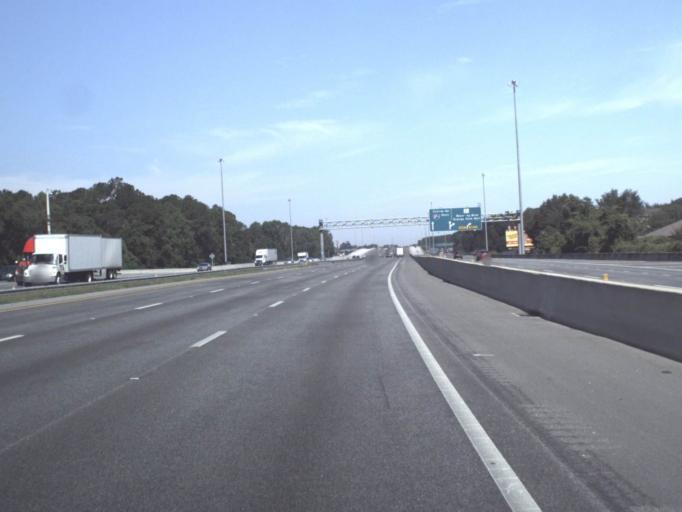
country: US
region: Florida
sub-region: Clay County
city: Bellair-Meadowbrook Terrace
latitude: 30.1923
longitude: -81.7274
